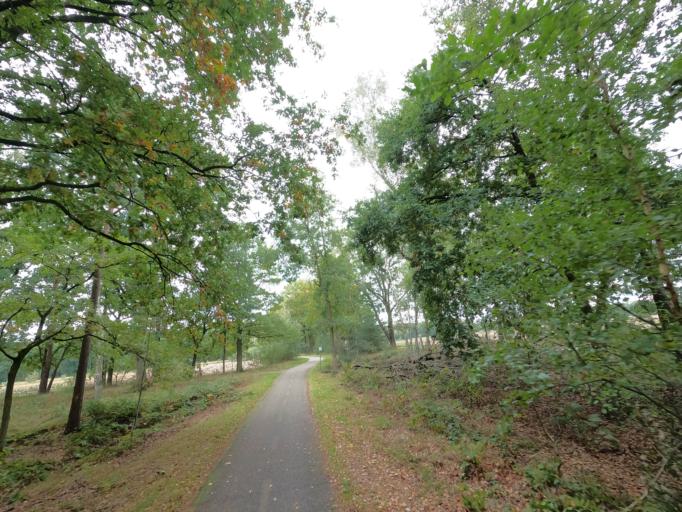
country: BE
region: Flanders
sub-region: Provincie Antwerpen
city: Retie
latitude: 51.2341
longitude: 5.0300
